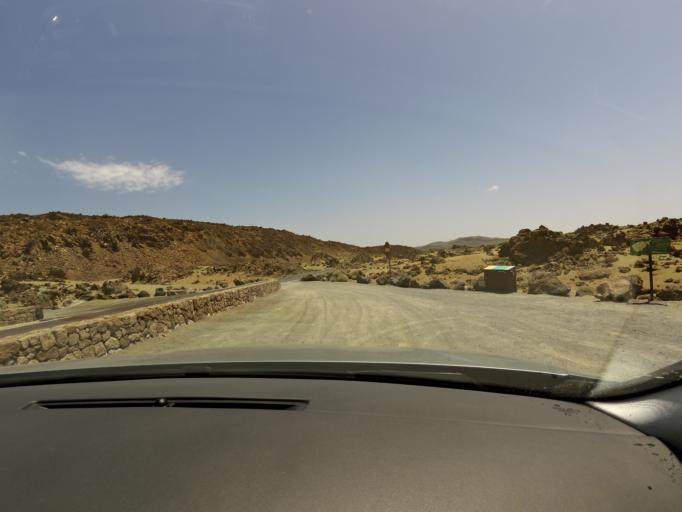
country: ES
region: Canary Islands
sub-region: Provincia de Santa Cruz de Tenerife
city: Los Realejos
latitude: 28.2658
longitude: -16.5885
